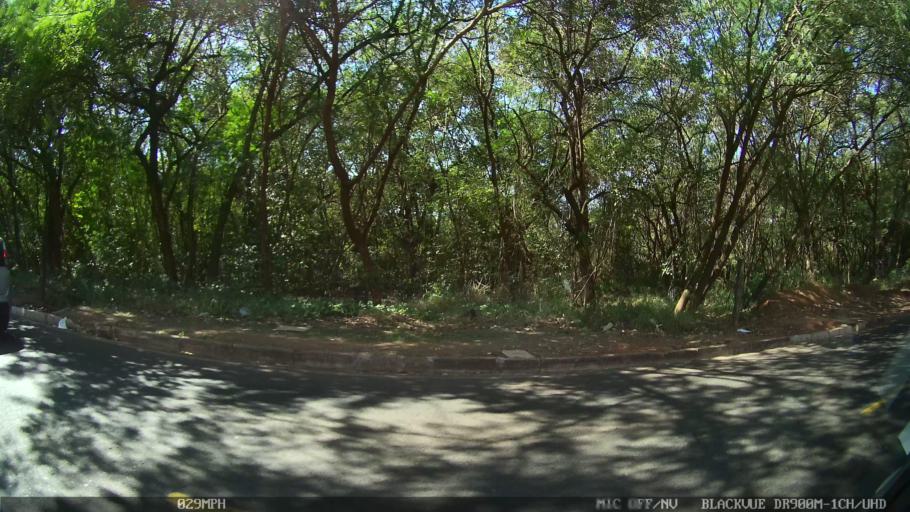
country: BR
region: Sao Paulo
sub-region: Sao Jose Do Rio Preto
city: Sao Jose do Rio Preto
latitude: -20.7808
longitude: -49.3835
